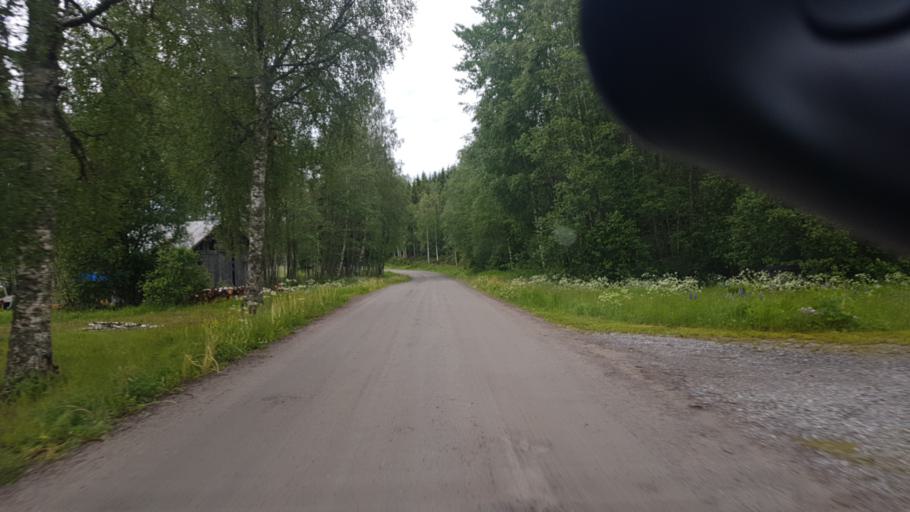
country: NO
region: Ostfold
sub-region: Romskog
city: Romskog
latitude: 59.6720
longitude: 11.9335
